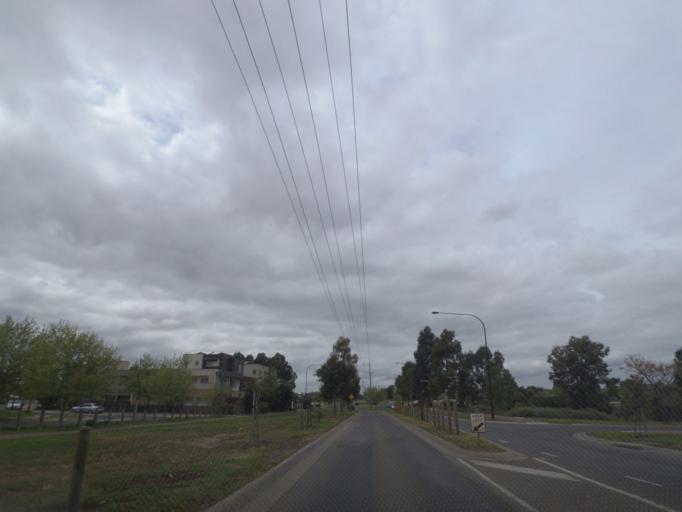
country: AU
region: Victoria
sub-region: Melton
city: Burnside Heights
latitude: -37.7221
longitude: 144.7360
